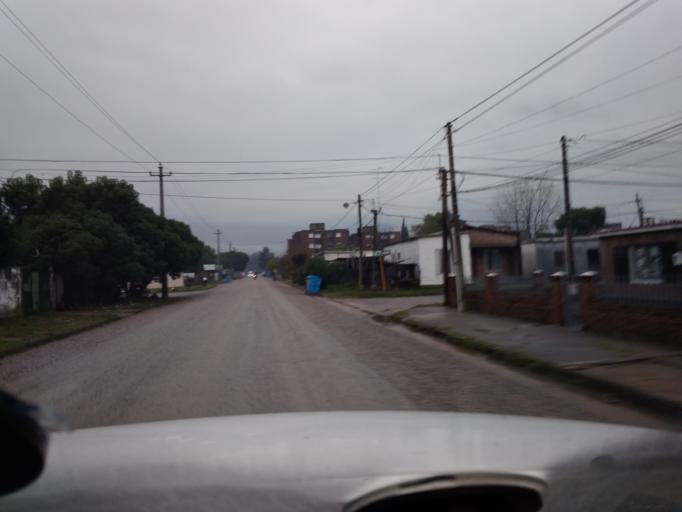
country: UY
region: Florida
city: Florida
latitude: -34.1076
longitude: -56.2114
